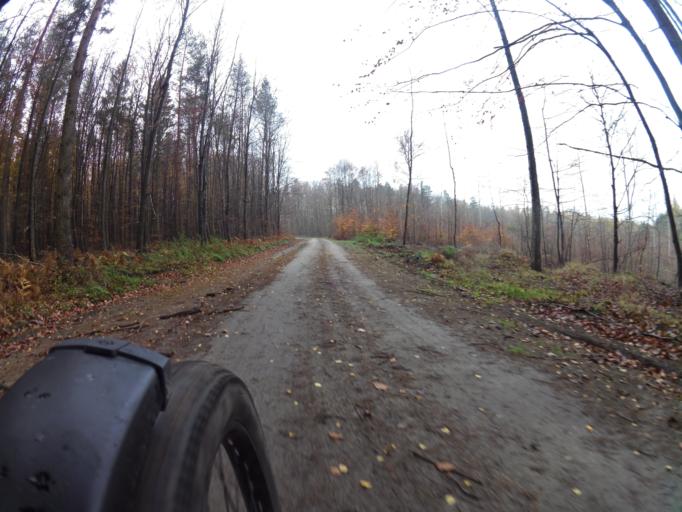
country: PL
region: Pomeranian Voivodeship
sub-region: Powiat pucki
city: Krokowa
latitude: 54.7719
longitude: 18.0931
